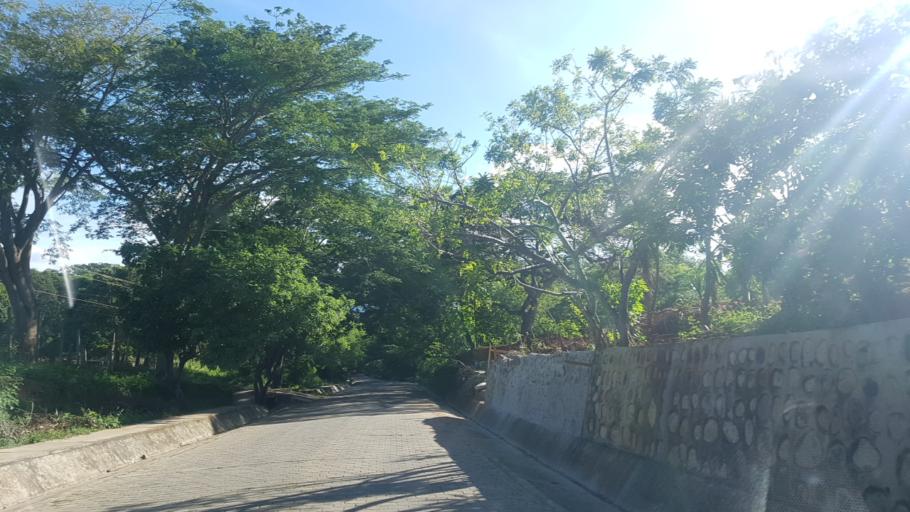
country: NI
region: Nueva Segovia
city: Mozonte
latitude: 13.6553
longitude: -86.4403
